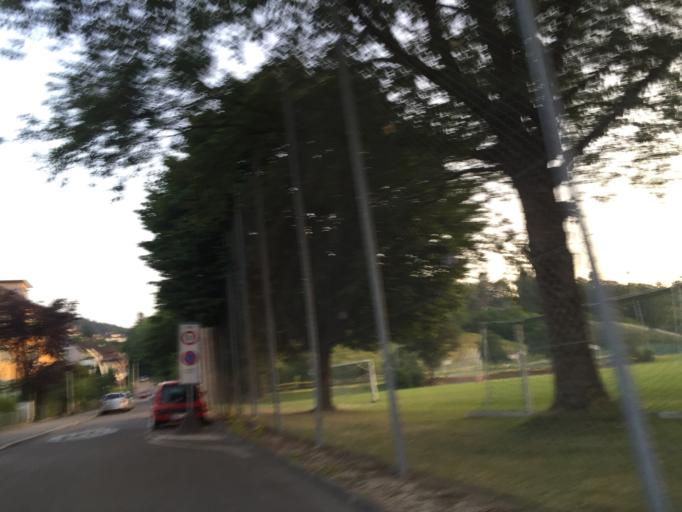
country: CH
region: Bern
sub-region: Bern-Mittelland District
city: Bern
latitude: 46.9304
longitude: 7.4384
